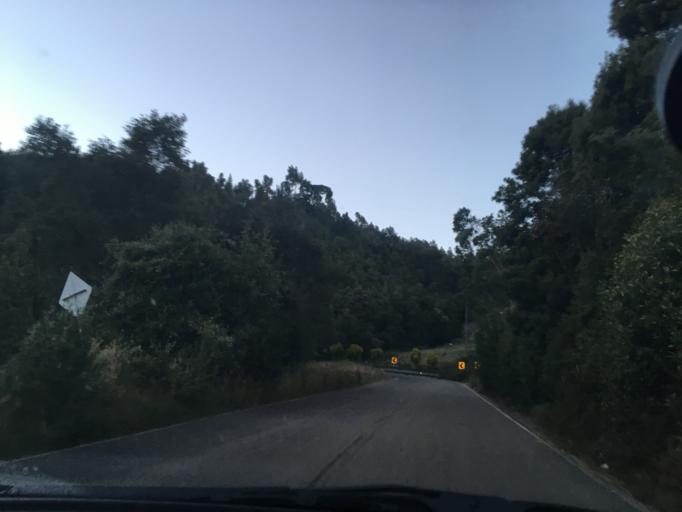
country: CO
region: Boyaca
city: Aquitania
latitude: 5.6116
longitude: -72.9081
